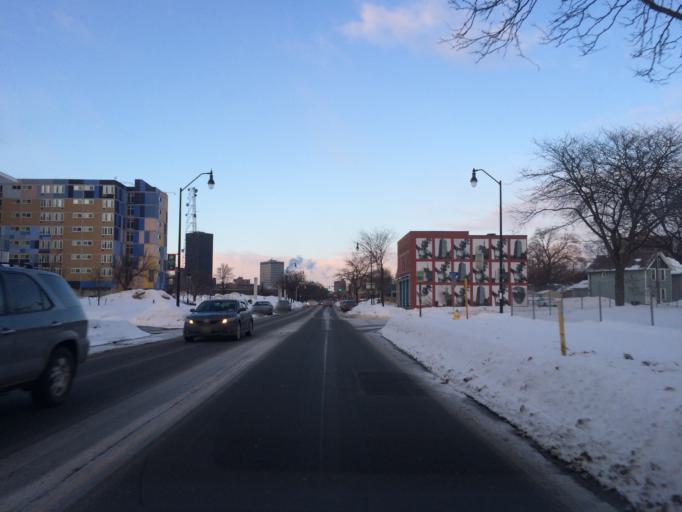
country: US
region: New York
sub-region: Monroe County
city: Rochester
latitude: 43.1445
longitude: -77.6106
